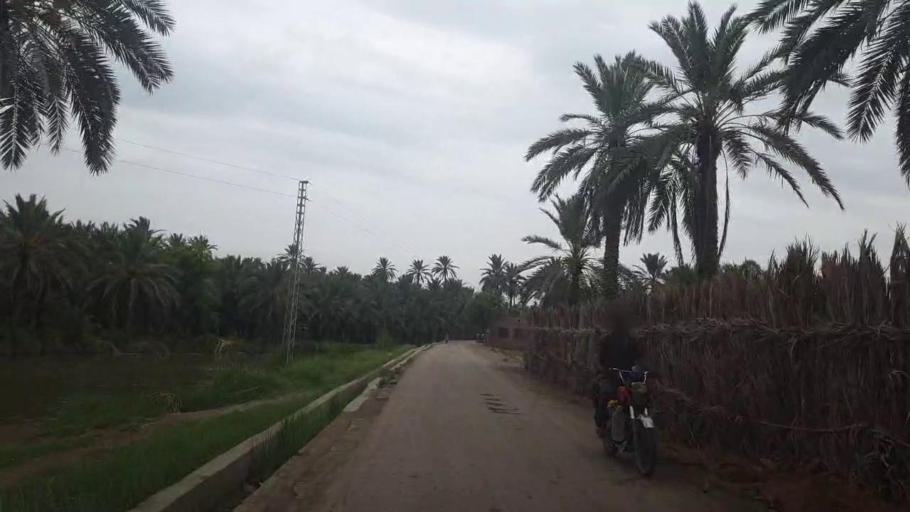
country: PK
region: Sindh
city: Khairpur
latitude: 27.5778
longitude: 68.7452
